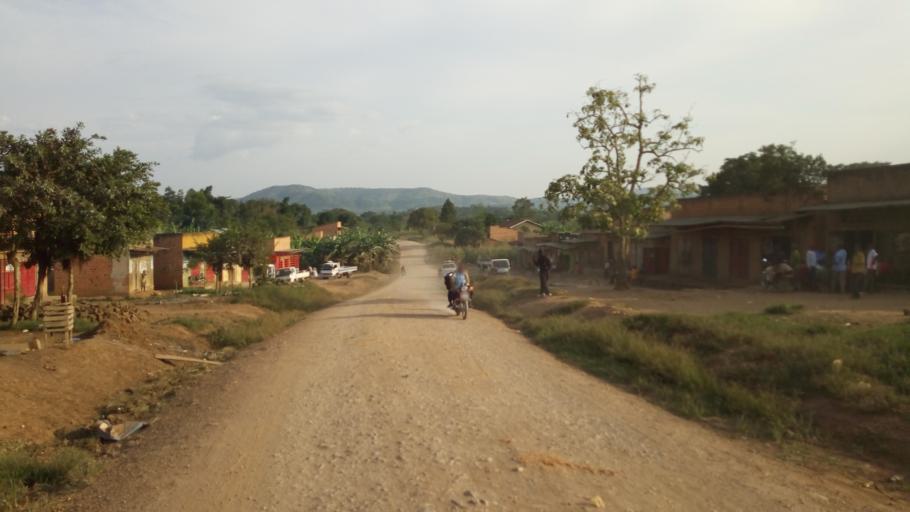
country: UG
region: Central Region
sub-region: Kiboga District
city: Kiboga
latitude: 0.7272
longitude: 31.7342
